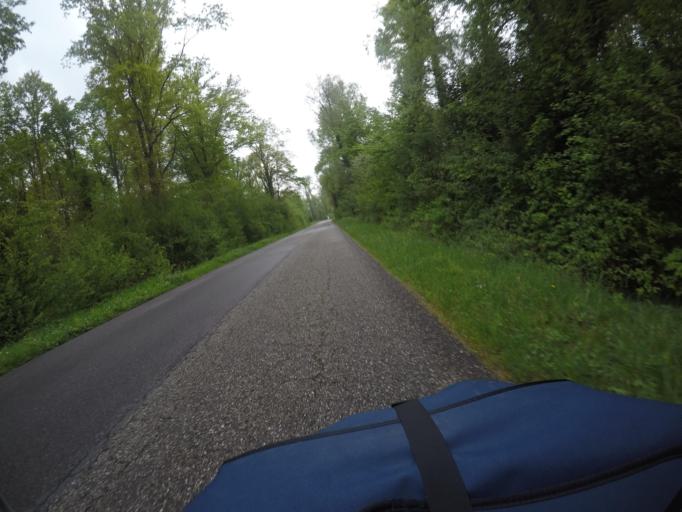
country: DE
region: Baden-Wuerttemberg
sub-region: Karlsruhe Region
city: Hugelsheim
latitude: 48.8416
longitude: 8.1045
